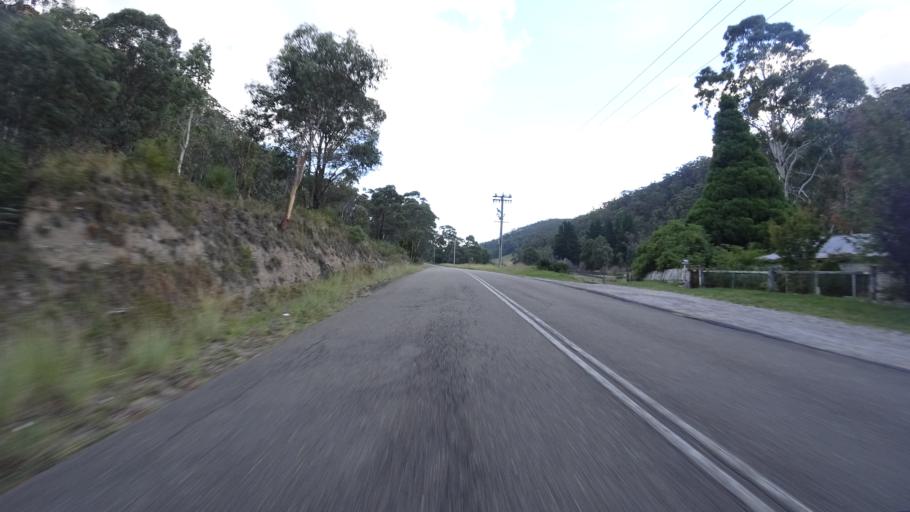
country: AU
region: New South Wales
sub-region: Lithgow
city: Lithgow
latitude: -33.4860
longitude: 150.1757
